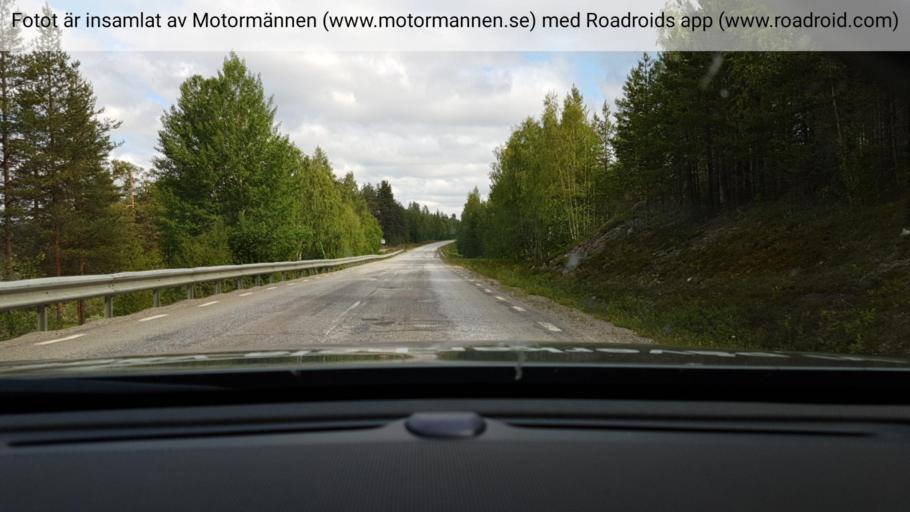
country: SE
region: Vaesterbotten
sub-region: Lycksele Kommun
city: Lycksele
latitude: 64.8662
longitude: 18.7212
